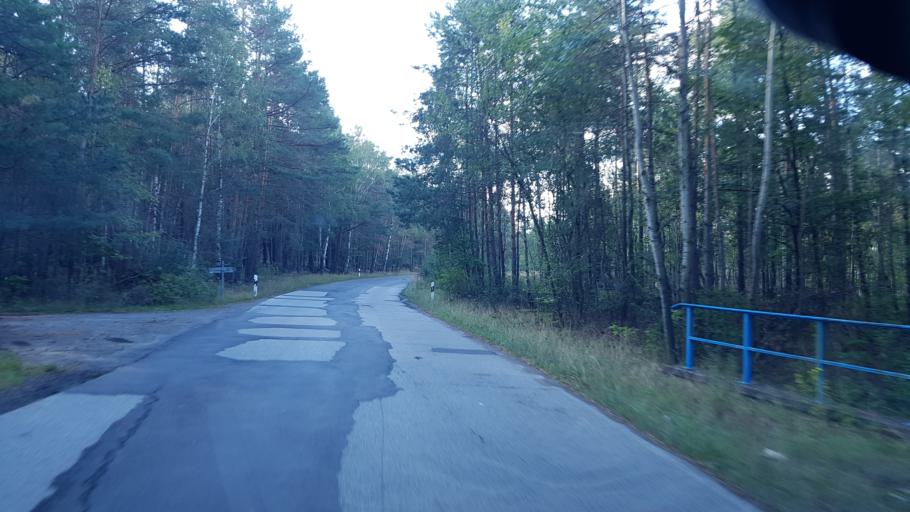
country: DE
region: Brandenburg
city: Spremberg
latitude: 51.5445
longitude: 14.2938
